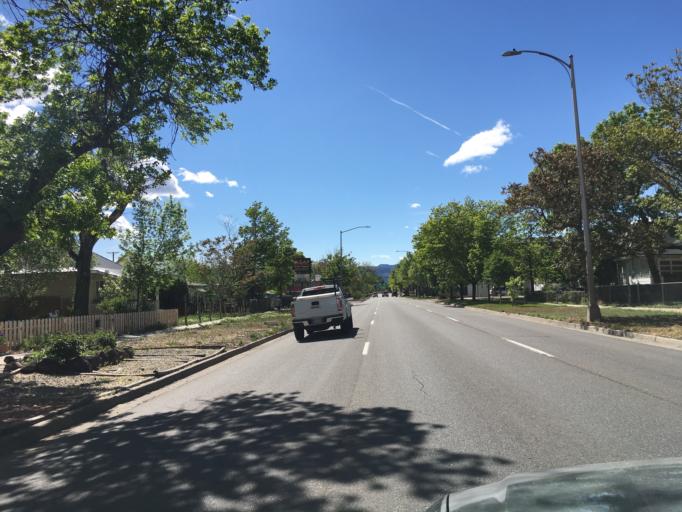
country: US
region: Colorado
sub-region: Mesa County
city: Grand Junction
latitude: 39.0654
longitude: -108.5582
